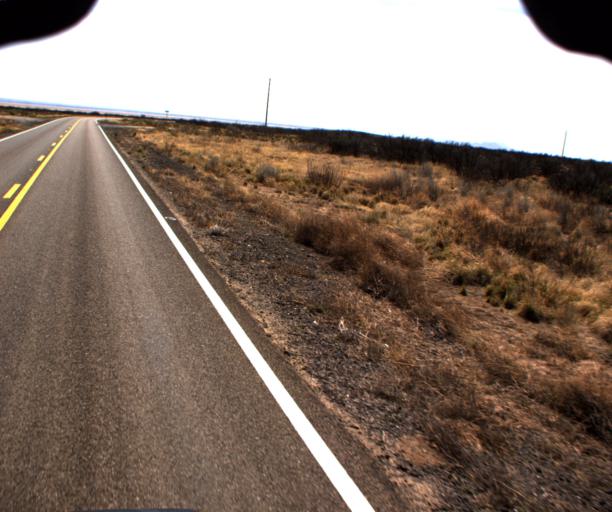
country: US
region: Arizona
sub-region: Cochise County
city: Willcox
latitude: 32.1393
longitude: -109.9198
